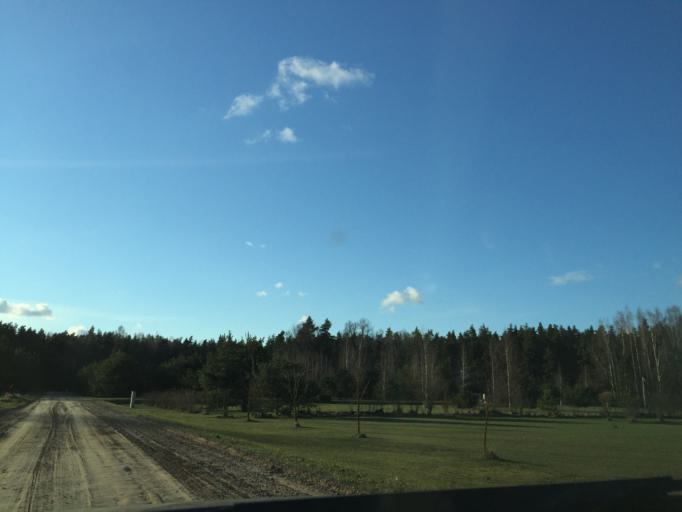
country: LV
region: Kekava
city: Kekava
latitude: 56.8526
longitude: 24.2357
